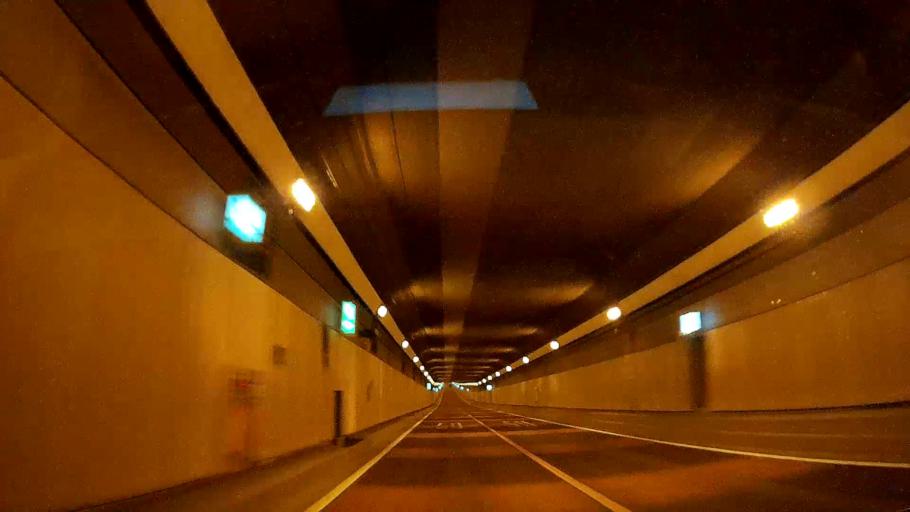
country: JP
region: Kanagawa
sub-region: Kawasaki-shi
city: Kawasaki
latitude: 35.6066
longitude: 139.7908
